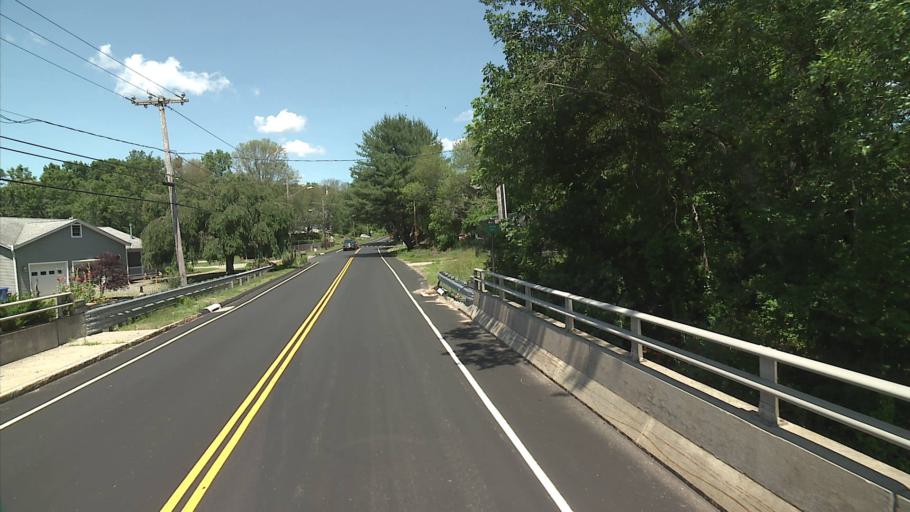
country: US
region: Connecticut
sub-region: New London County
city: Preston City
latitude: 41.5566
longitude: -71.8892
